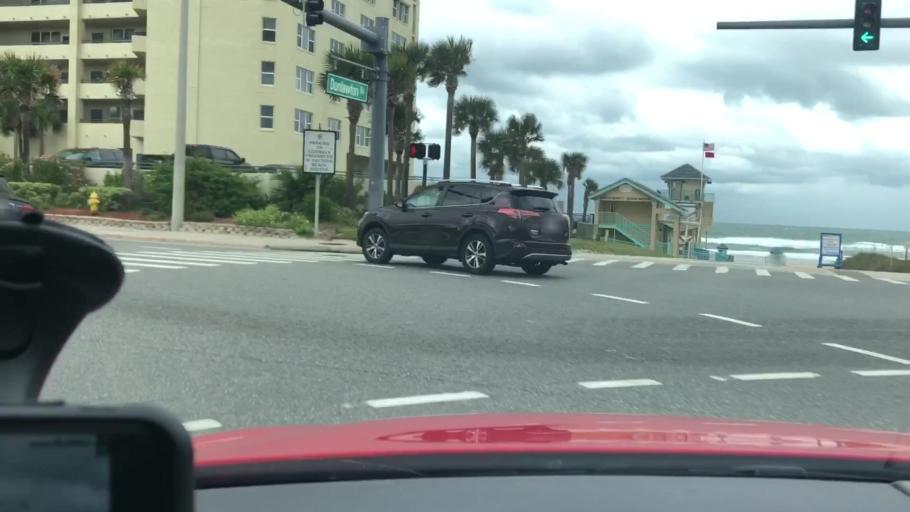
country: US
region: Florida
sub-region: Volusia County
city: Daytona Beach Shores
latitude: 29.1512
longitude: -80.9691
